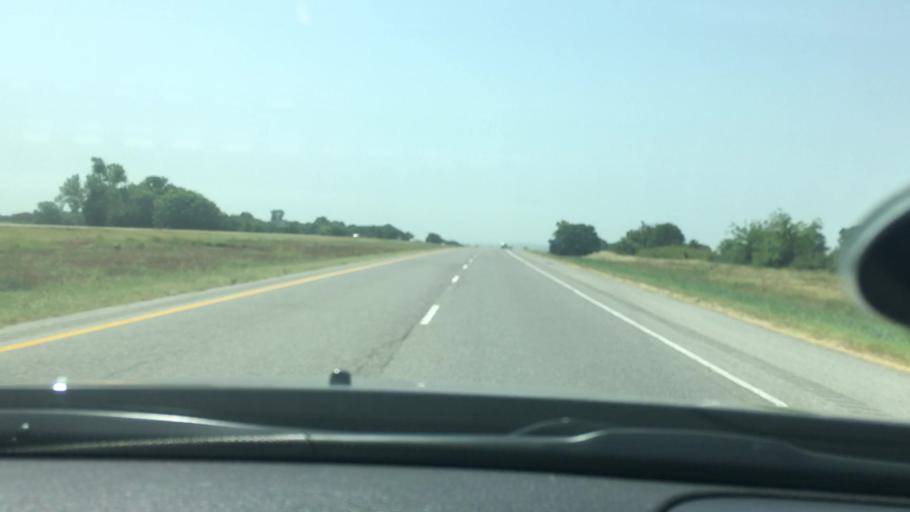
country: US
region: Oklahoma
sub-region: Garvin County
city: Wynnewood
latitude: 34.5591
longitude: -97.1935
